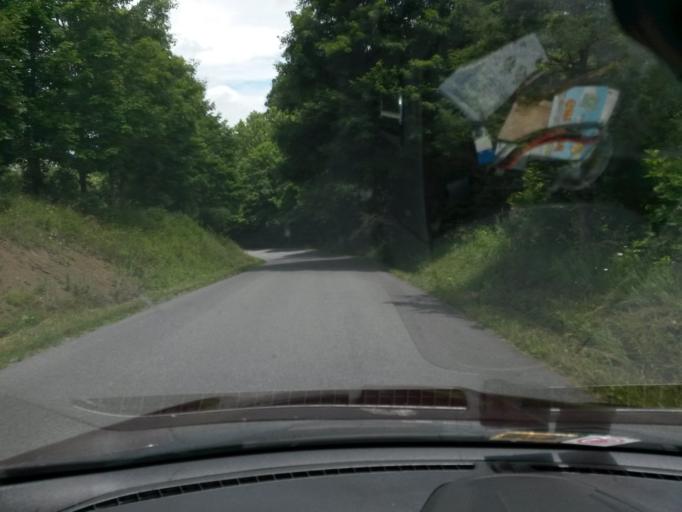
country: US
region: West Virginia
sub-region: Monroe County
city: Union
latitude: 37.5219
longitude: -80.5575
